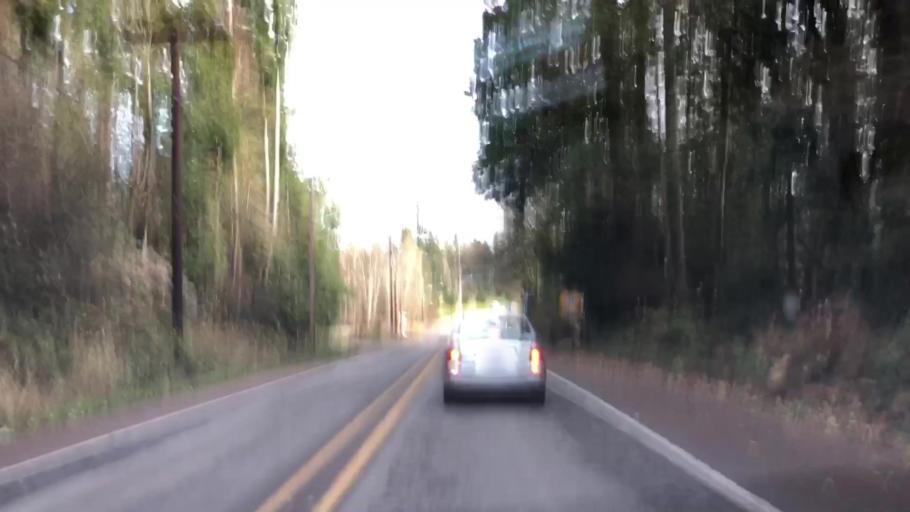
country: US
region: Washington
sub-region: Kitsap County
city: Suquamish
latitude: 47.7274
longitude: -122.5621
